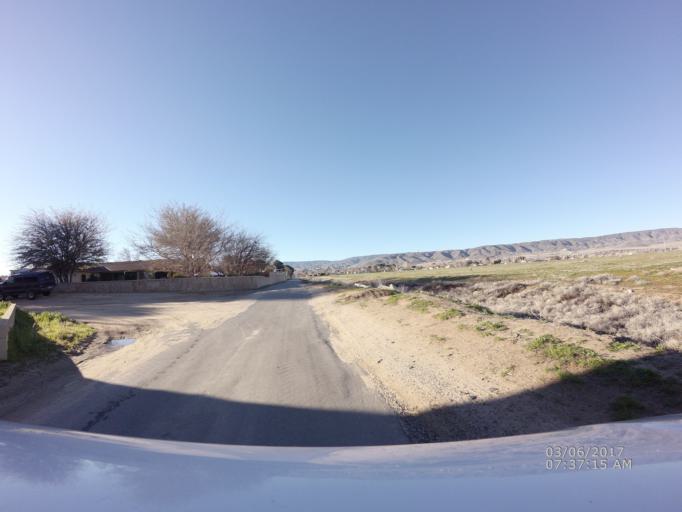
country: US
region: California
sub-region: Los Angeles County
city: Quartz Hill
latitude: 34.6640
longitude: -118.2232
